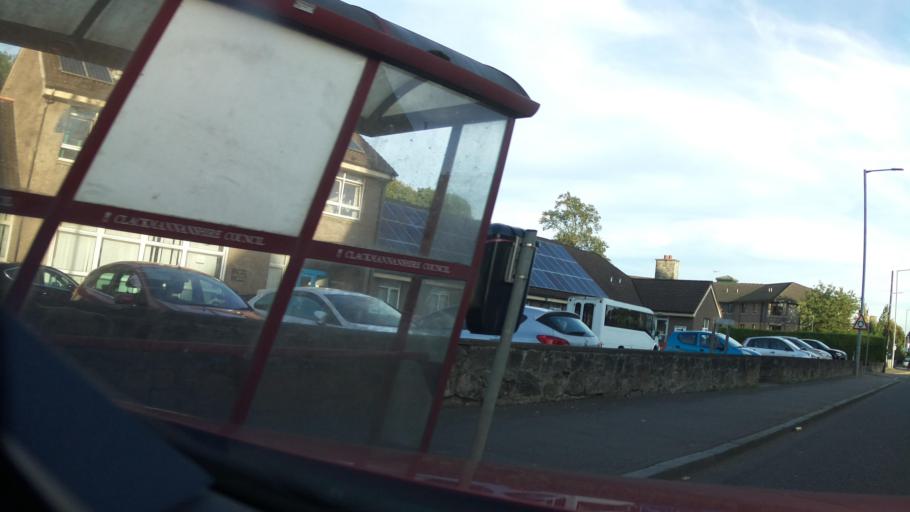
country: GB
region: Scotland
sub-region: Clackmannanshire
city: Alloa
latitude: 56.1187
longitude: -3.7970
